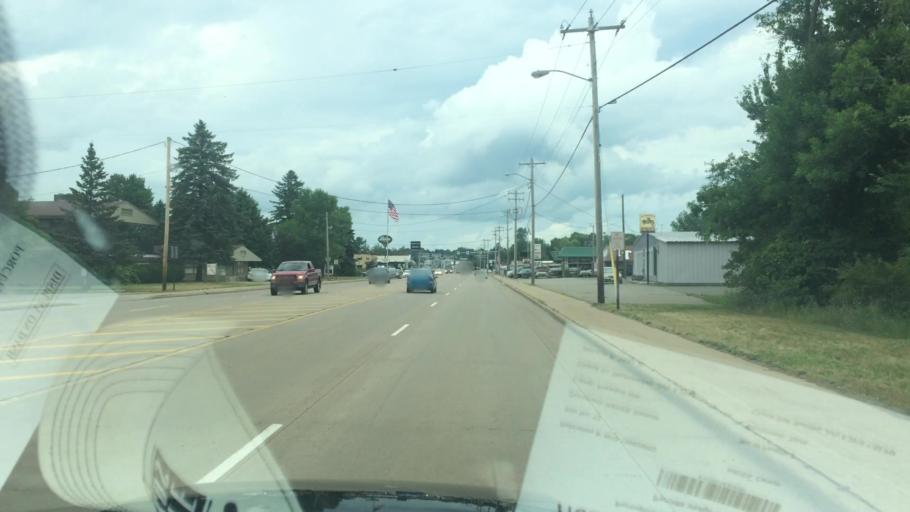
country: US
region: Wisconsin
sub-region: Marathon County
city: Schofield
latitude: 44.9230
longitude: -89.6131
